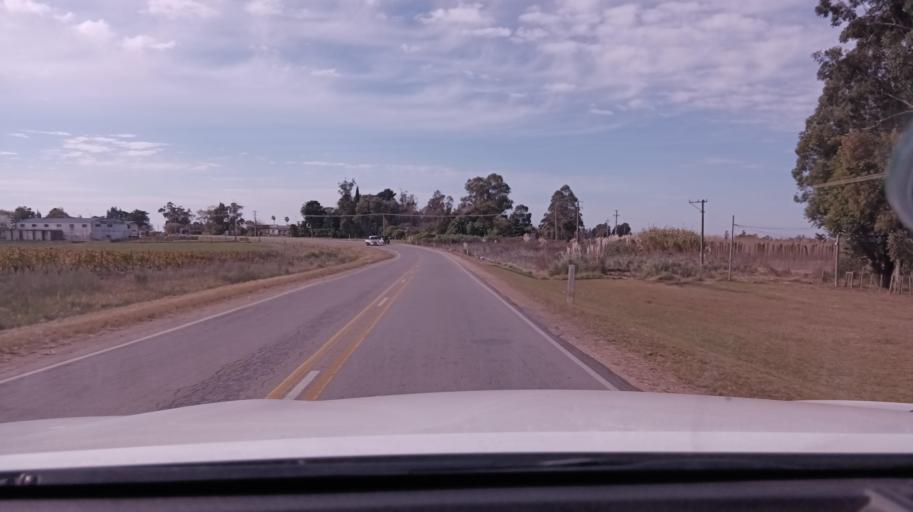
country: UY
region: Canelones
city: Toledo
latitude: -34.7078
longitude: -56.1067
